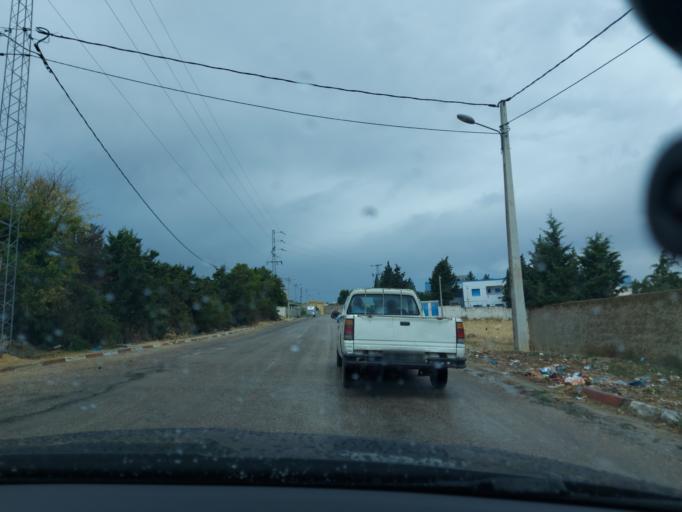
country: TN
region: Silyanah
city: Maktar
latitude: 35.8530
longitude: 9.2138
